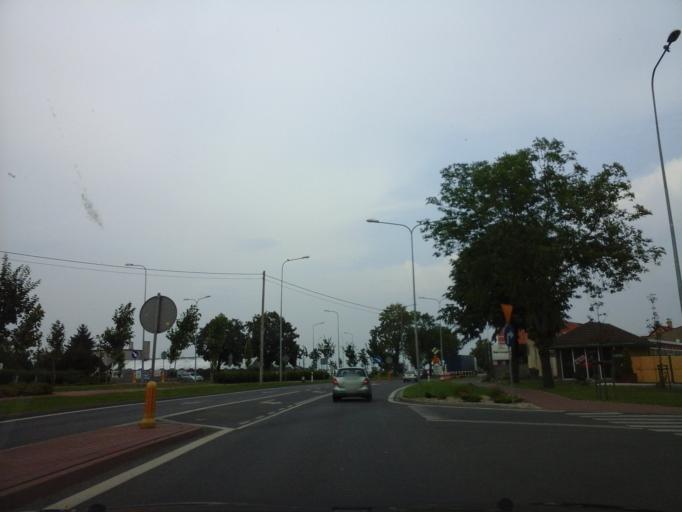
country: PL
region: Greater Poland Voivodeship
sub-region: Powiat grodziski
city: Grodzisk Wielkopolski
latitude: 52.2220
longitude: 16.3738
